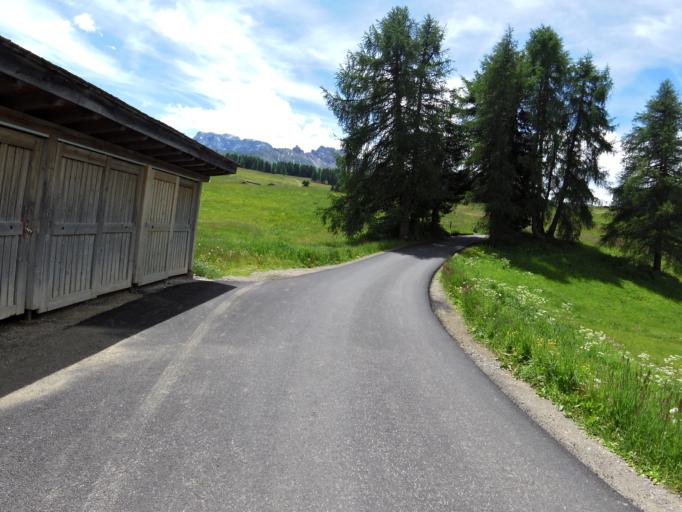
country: IT
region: Trentino-Alto Adige
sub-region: Bolzano
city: Ortisei
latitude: 46.5423
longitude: 11.6455
